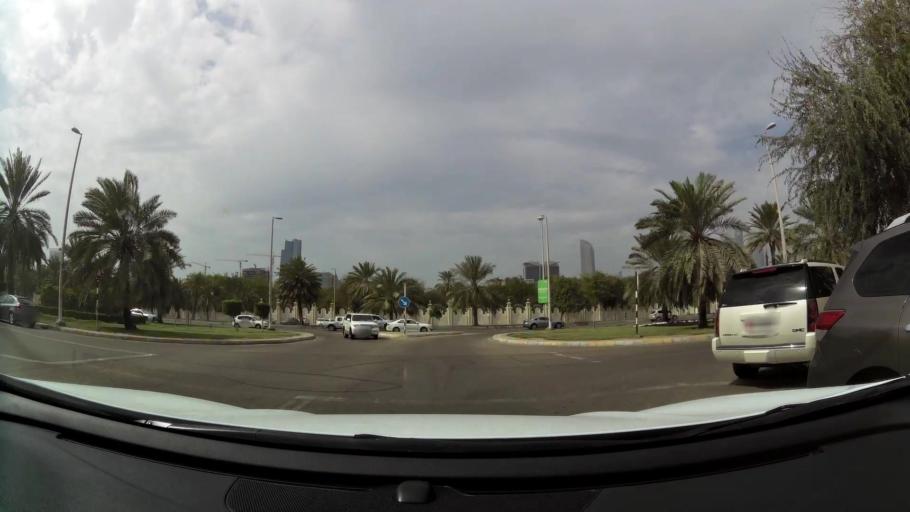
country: AE
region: Abu Dhabi
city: Abu Dhabi
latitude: 24.4689
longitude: 54.3574
